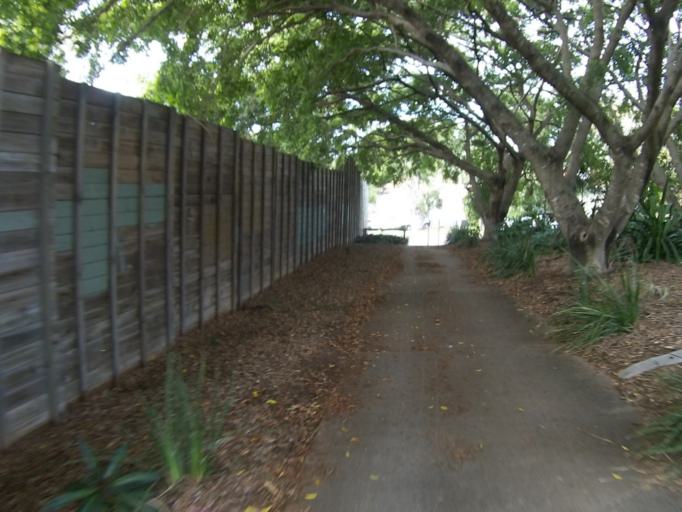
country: AU
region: Queensland
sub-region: Brisbane
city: Greenslopes
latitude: -27.5210
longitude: 153.0519
